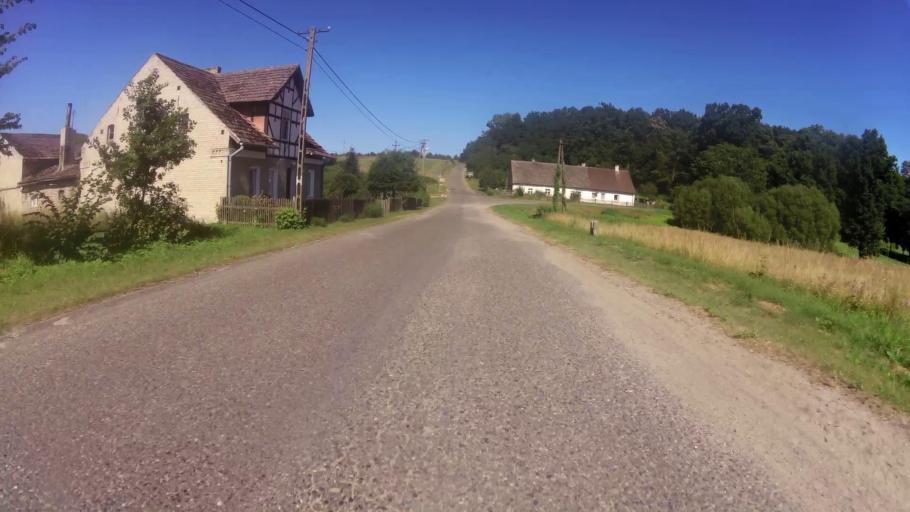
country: PL
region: West Pomeranian Voivodeship
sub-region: Powiat stargardzki
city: Insko
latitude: 53.4448
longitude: 15.6453
